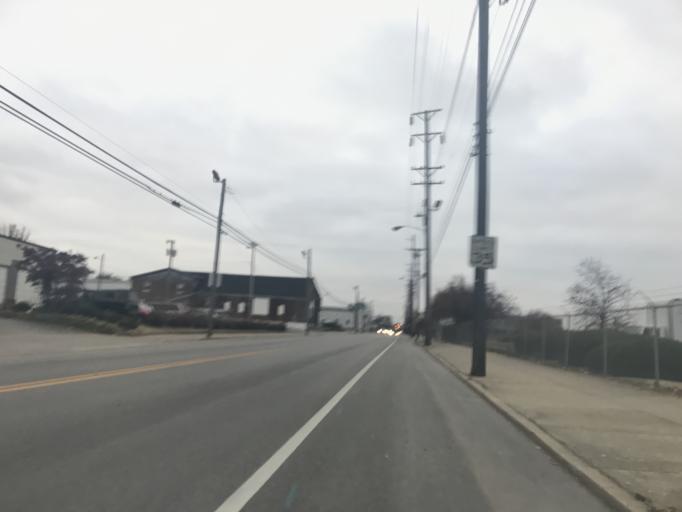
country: US
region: Kentucky
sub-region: Jefferson County
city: Louisville
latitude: 38.2392
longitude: -85.7732
